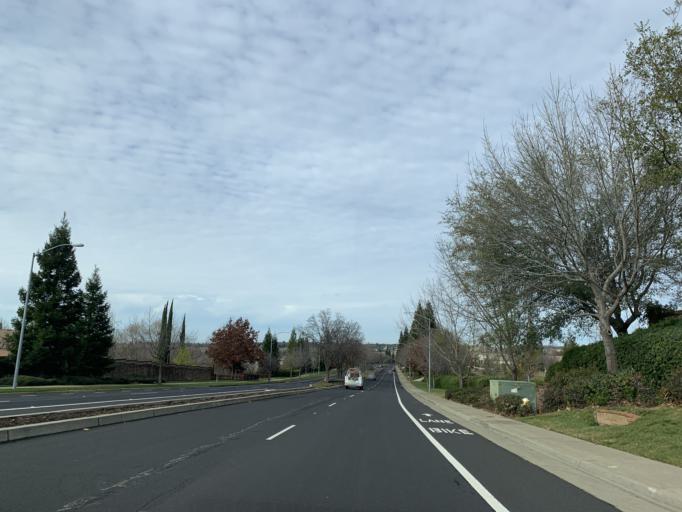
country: US
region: California
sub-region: El Dorado County
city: El Dorado Hills
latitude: 38.6732
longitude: -121.1023
